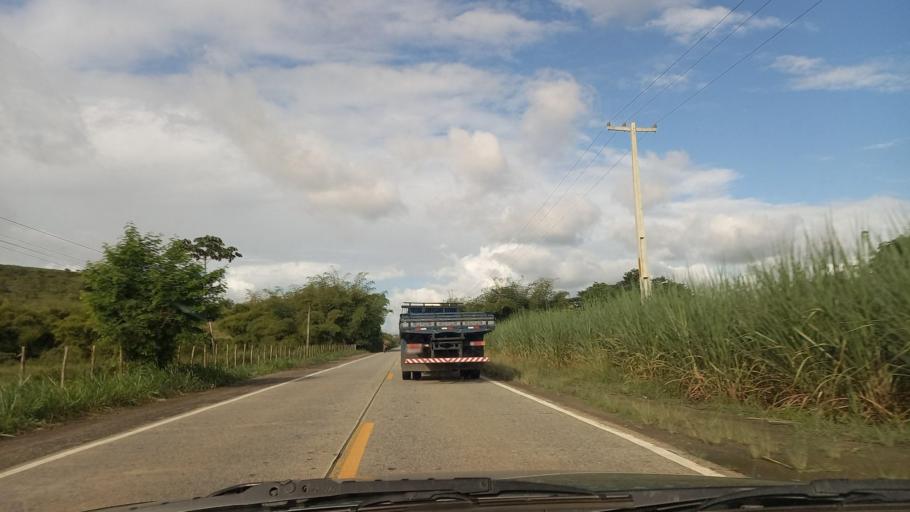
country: BR
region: Pernambuco
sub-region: Palmares
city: Palmares
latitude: -8.6915
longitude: -35.6289
